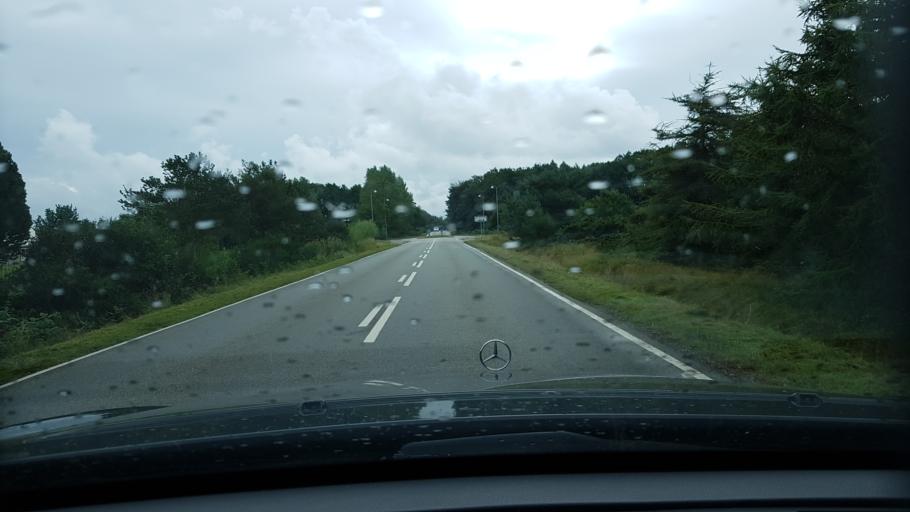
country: DK
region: North Denmark
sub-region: Alborg Kommune
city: Hals
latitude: 56.8214
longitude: 10.2695
